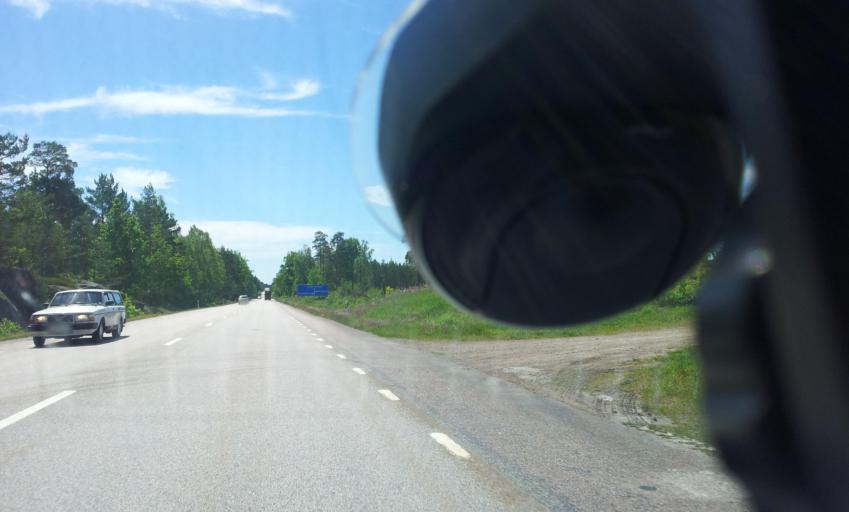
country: SE
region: Kalmar
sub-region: Oskarshamns Kommun
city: Oskarshamn
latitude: 57.4837
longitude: 16.5180
